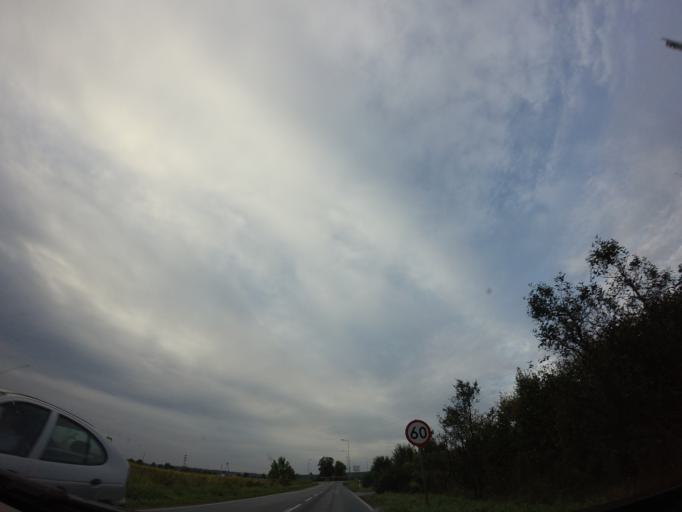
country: PL
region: Lubusz
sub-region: Powiat strzelecko-drezdenecki
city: Drezdenko
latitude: 52.8253
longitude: 15.8279
